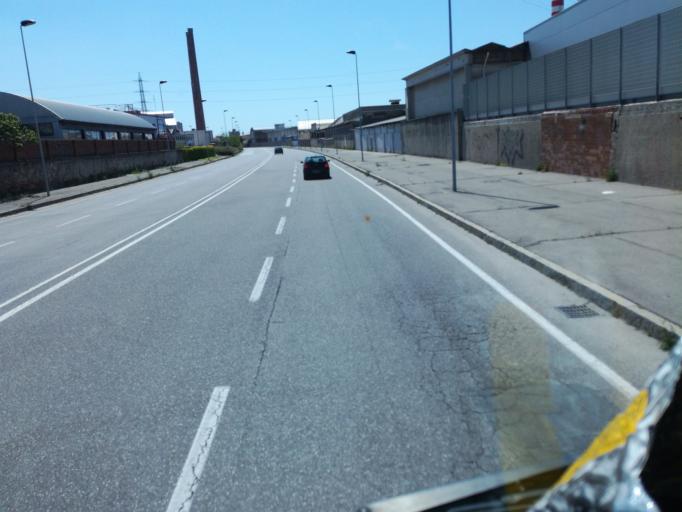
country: IT
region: Tuscany
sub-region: Provincia di Livorno
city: Livorno
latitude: 43.5696
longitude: 10.3147
